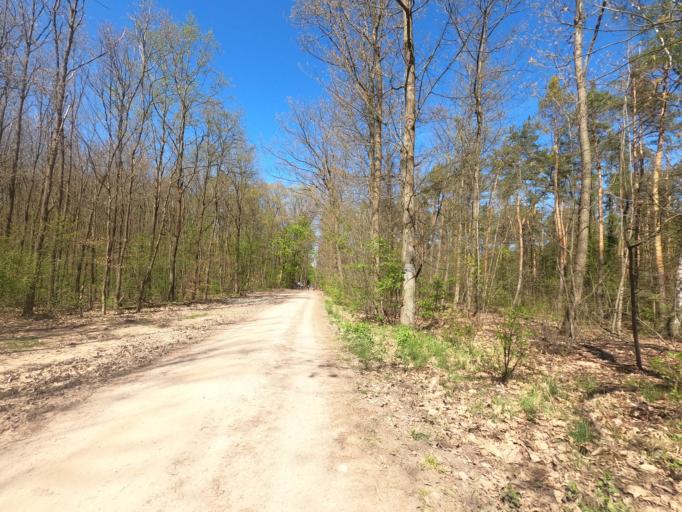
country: DE
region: Hesse
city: Morfelden-Walldorf
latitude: 49.9625
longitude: 8.5936
